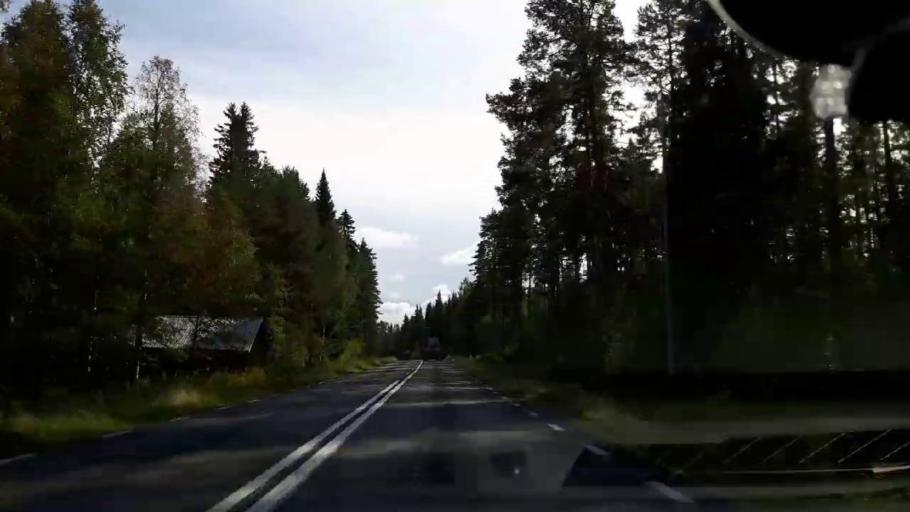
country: SE
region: Jaemtland
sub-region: Braecke Kommun
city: Braecke
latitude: 63.1704
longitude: 15.5461
